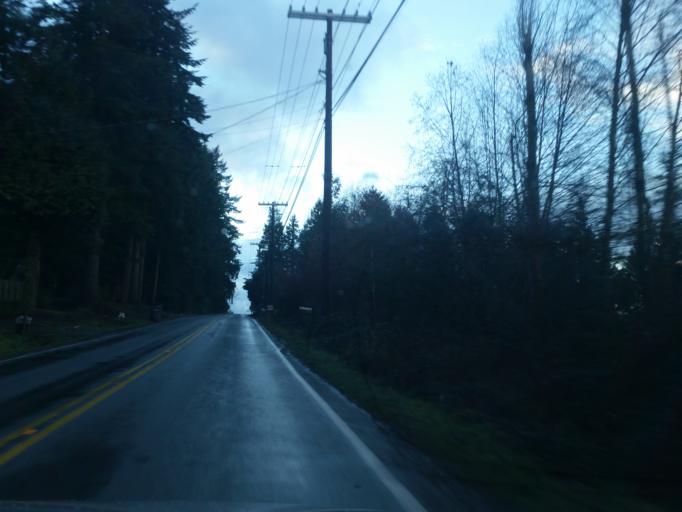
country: US
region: Washington
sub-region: Snohomish County
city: Cathcart
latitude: 47.8337
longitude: -122.0978
